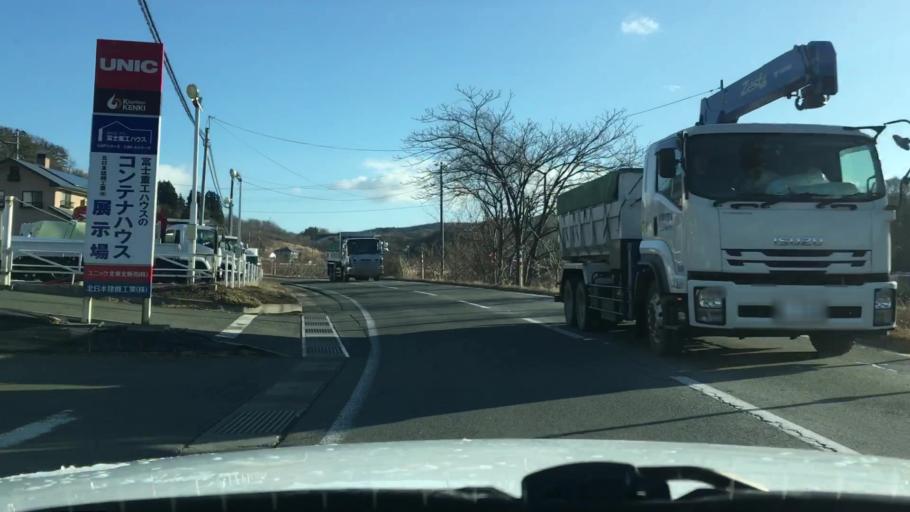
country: JP
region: Iwate
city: Morioka-shi
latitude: 39.6617
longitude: 141.1974
